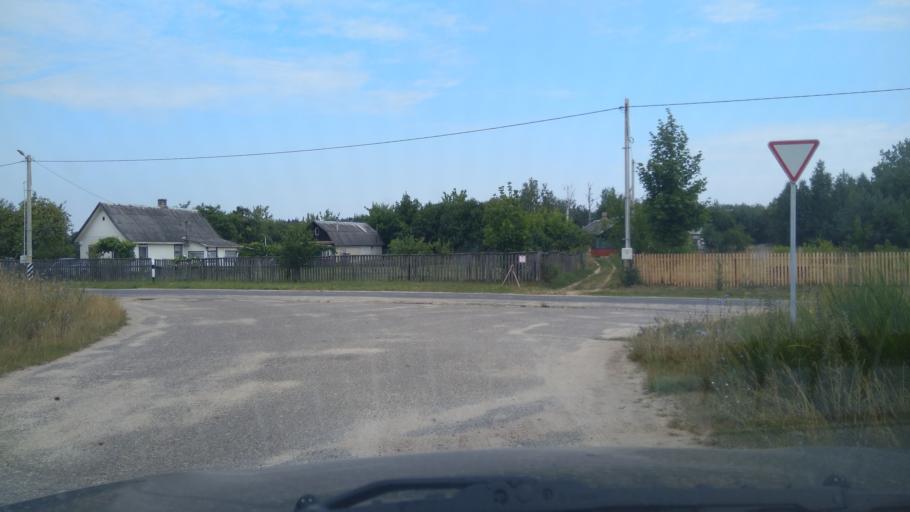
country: BY
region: Brest
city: Nyakhachava
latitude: 52.6086
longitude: 25.0921
